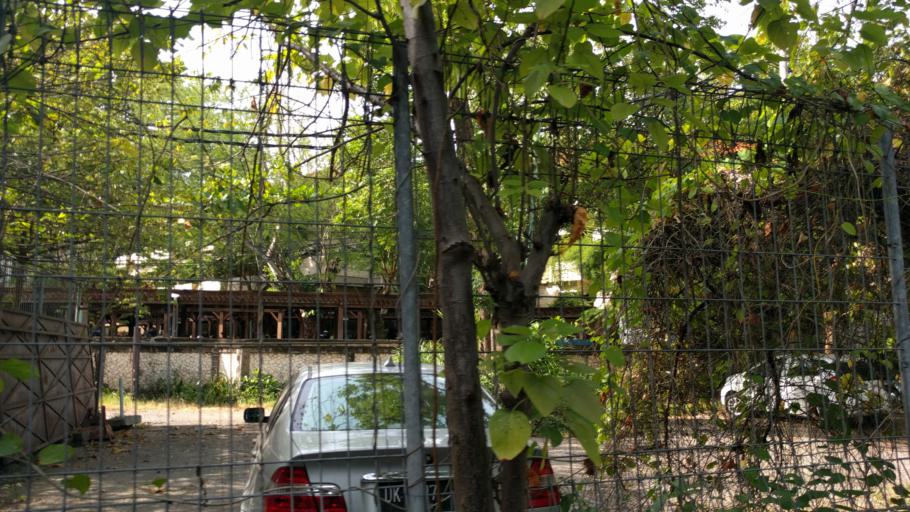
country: ID
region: Bali
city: Kuta
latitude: -8.6906
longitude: 115.1598
